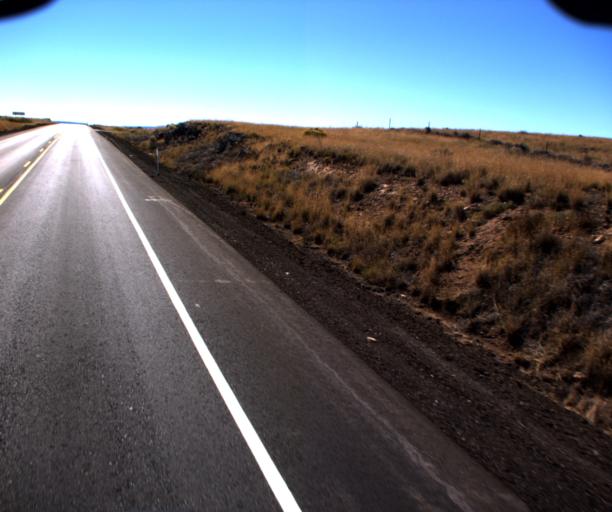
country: US
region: Arizona
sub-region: Apache County
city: Springerville
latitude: 34.2453
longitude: -109.3485
